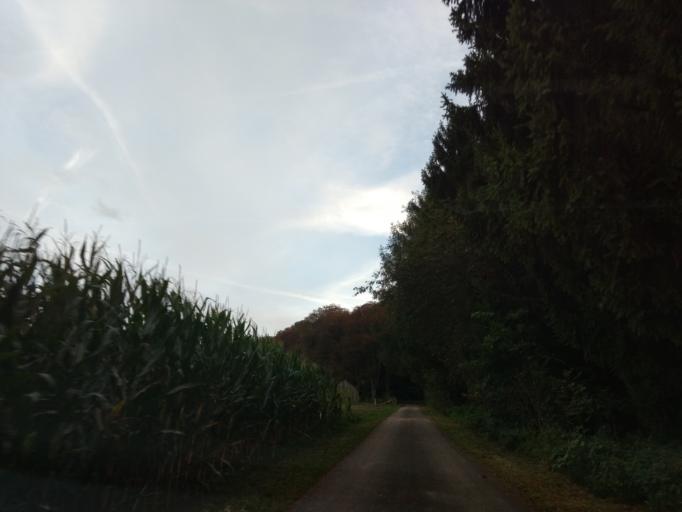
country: DE
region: North Rhine-Westphalia
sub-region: Regierungsbezirk Detmold
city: Paderborn
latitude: 51.6686
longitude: 8.7952
